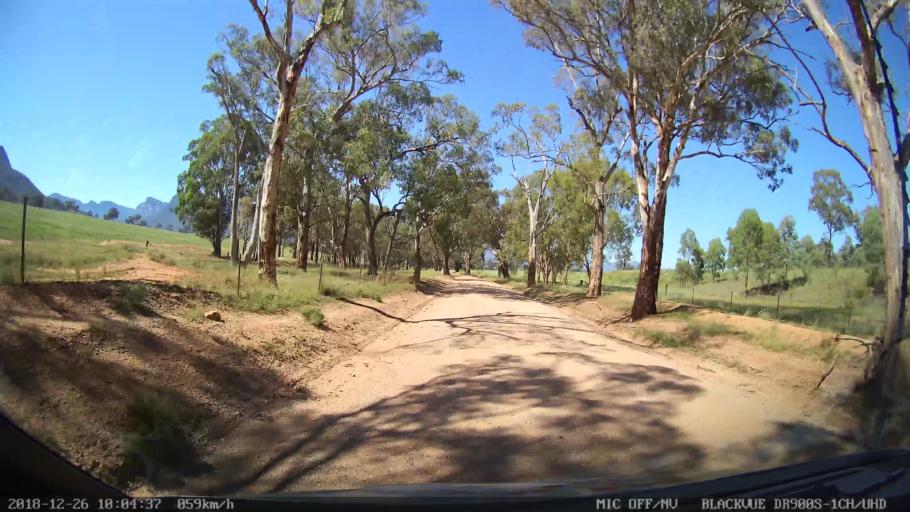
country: AU
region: New South Wales
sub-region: Mid-Western Regional
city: Kandos
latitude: -33.0717
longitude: 150.2135
